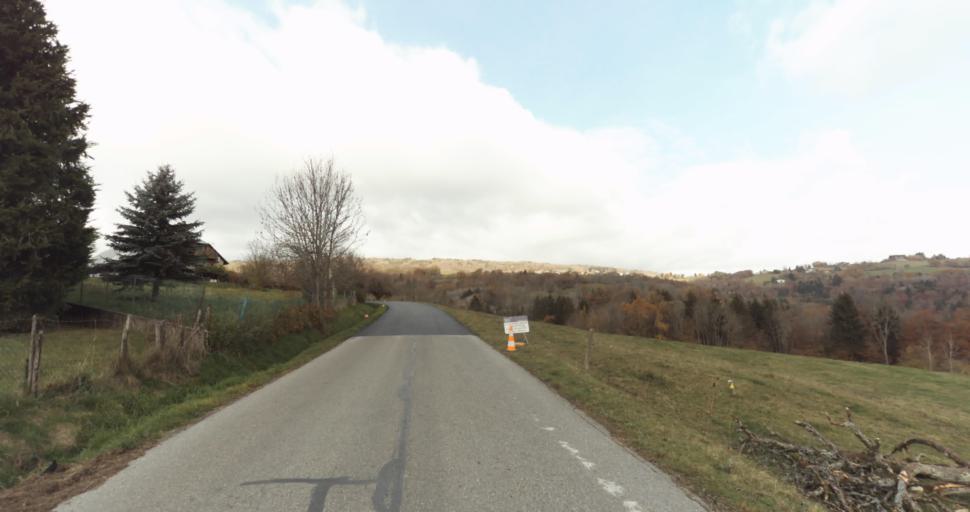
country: FR
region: Rhone-Alpes
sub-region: Departement de la Haute-Savoie
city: Epagny
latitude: 45.9632
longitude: 6.1019
